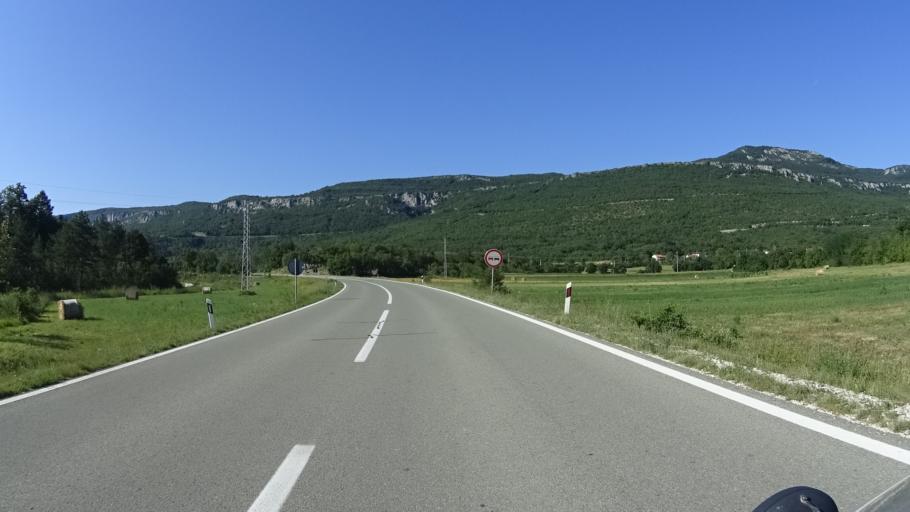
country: HR
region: Istarska
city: Lovran
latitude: 45.3168
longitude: 14.1394
